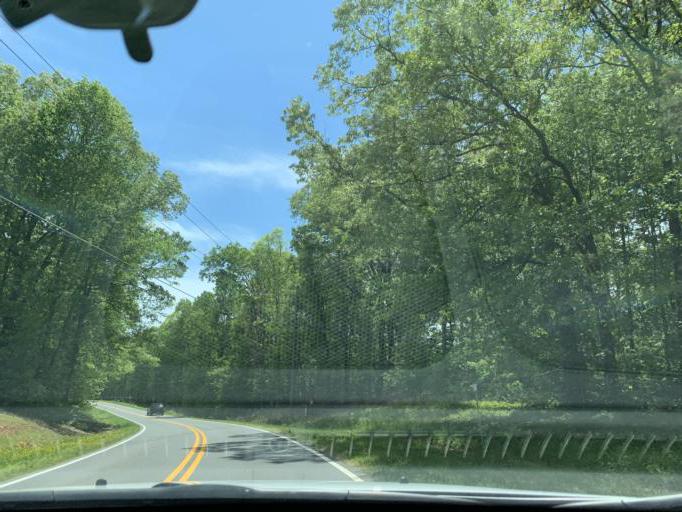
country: US
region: Georgia
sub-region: Hall County
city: Flowery Branch
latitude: 34.2542
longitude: -84.0249
